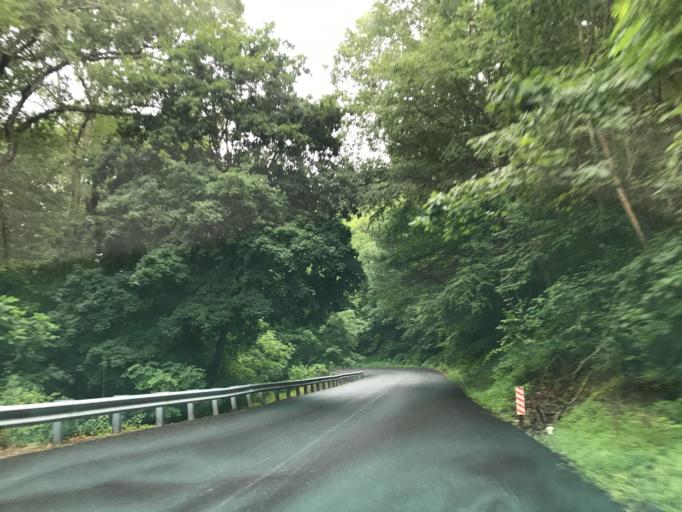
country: US
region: Pennsylvania
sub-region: York County
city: New Freedom
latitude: 39.6800
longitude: -76.7730
